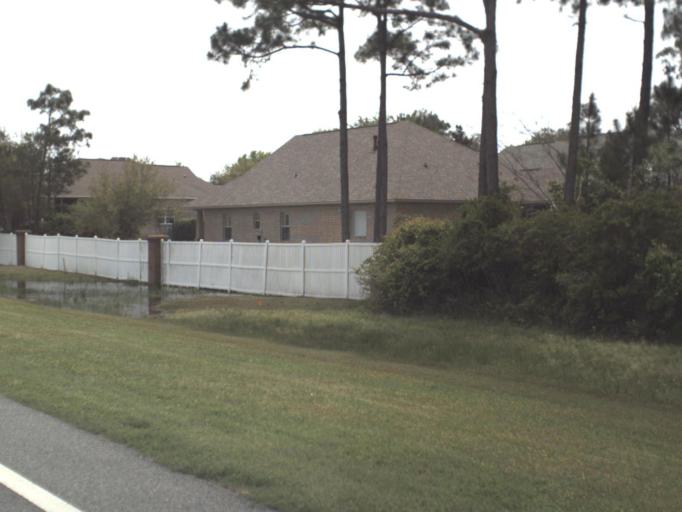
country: US
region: Florida
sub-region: Escambia County
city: Warrington
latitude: 30.3381
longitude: -87.3460
